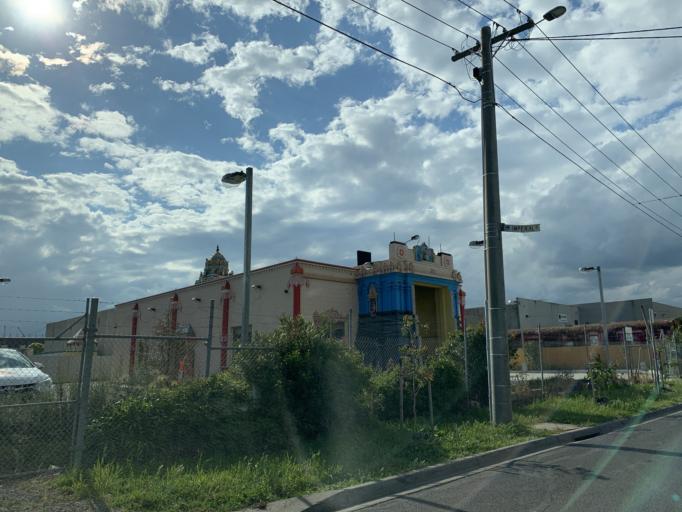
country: AU
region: Victoria
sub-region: Brimbank
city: Albion
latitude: -37.7565
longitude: 144.8368
